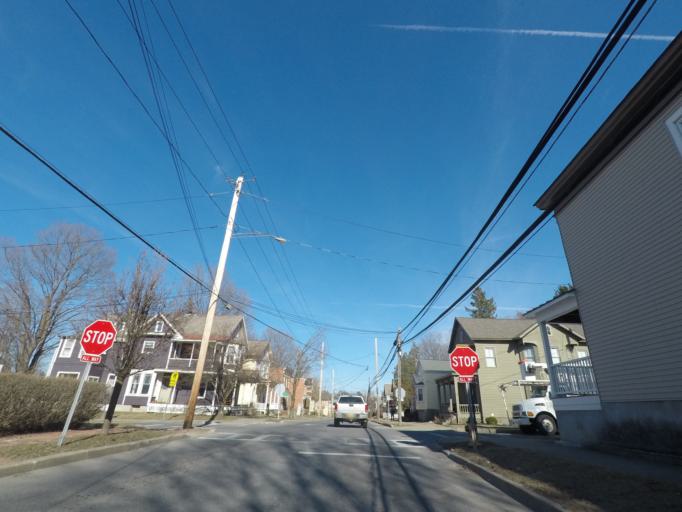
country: US
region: New York
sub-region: Saratoga County
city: Saratoga Springs
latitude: 43.0802
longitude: -73.7963
